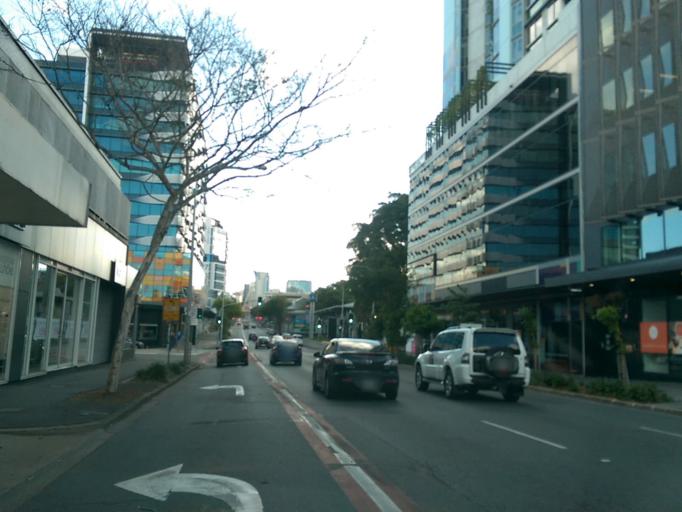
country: AU
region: Queensland
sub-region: Brisbane
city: Fortitude Valley
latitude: -27.4548
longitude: 153.0387
